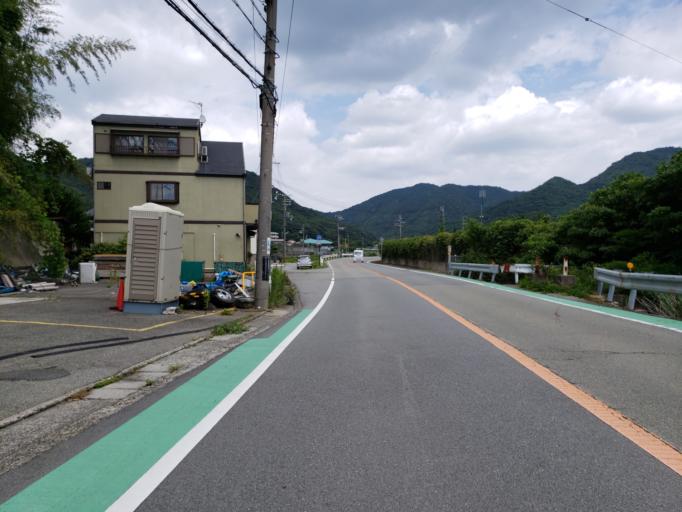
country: JP
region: Hyogo
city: Aioi
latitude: 34.7875
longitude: 134.4770
